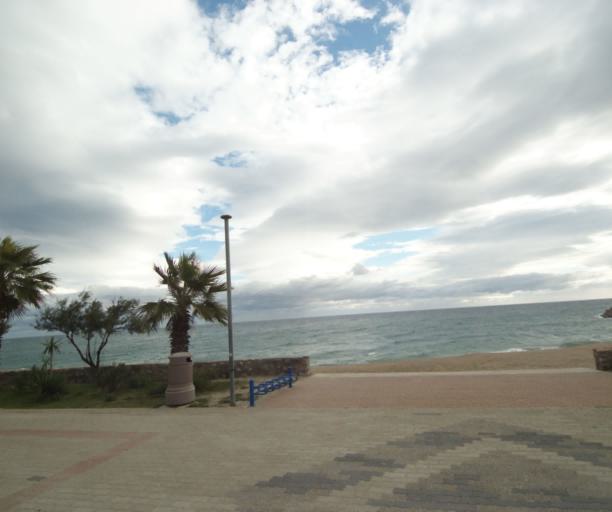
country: FR
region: Languedoc-Roussillon
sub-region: Departement des Pyrenees-Orientales
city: Argelers
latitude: 42.5440
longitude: 3.0513
